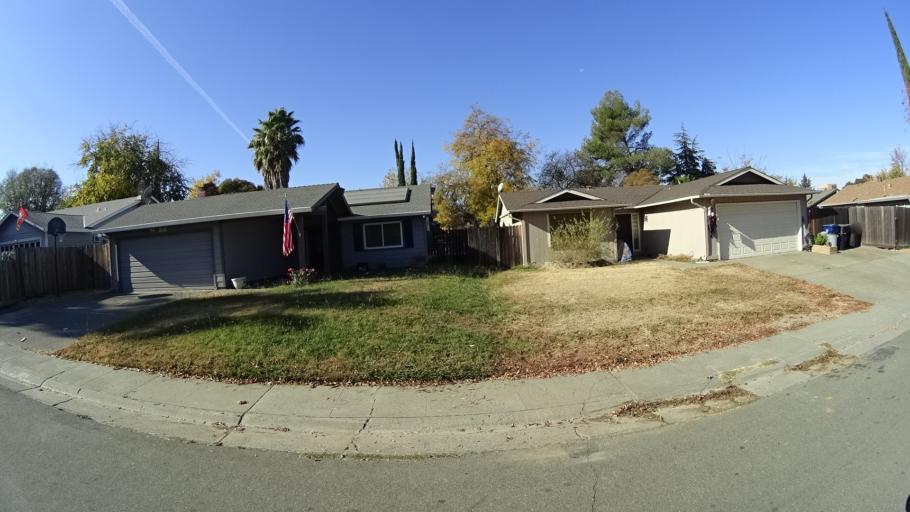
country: US
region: California
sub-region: Sacramento County
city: Antelope
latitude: 38.7129
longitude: -121.3163
